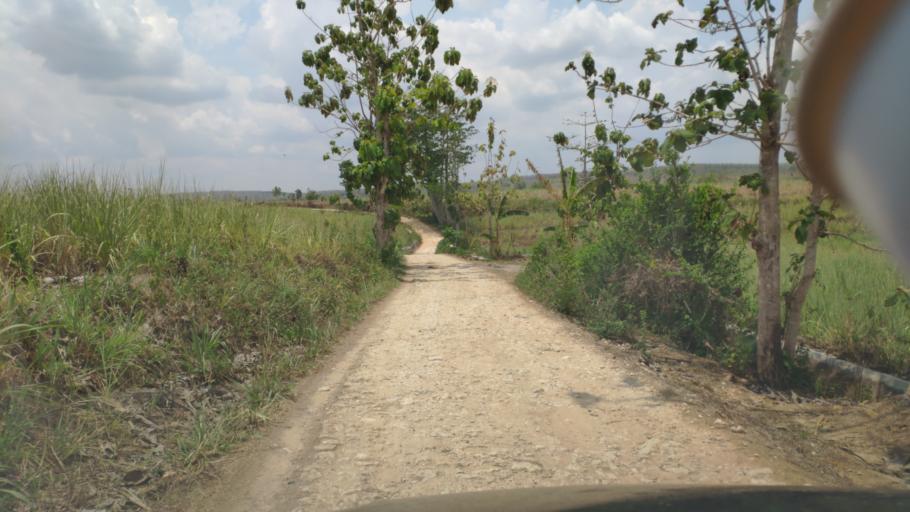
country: ID
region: Central Java
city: Ngapus
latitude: -6.9689
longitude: 111.2169
